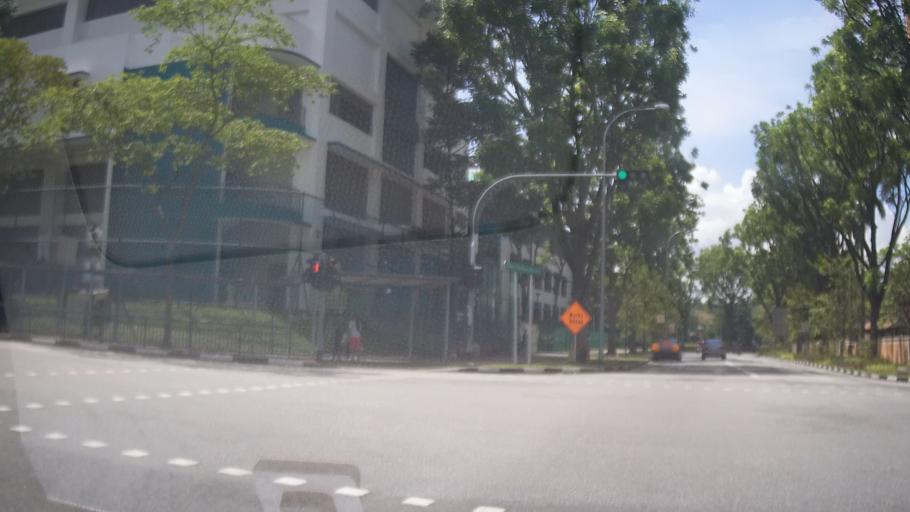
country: MY
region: Johor
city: Johor Bahru
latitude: 1.3963
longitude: 103.7500
